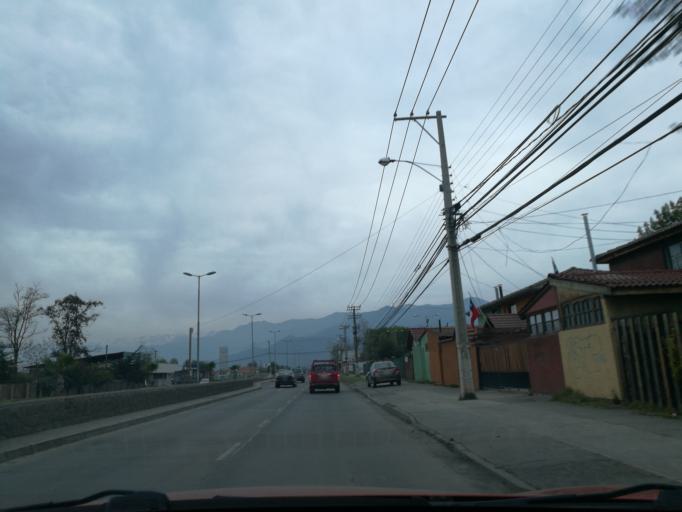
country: CL
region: O'Higgins
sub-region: Provincia de Cachapoal
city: Machali
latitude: -34.1728
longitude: -70.6865
